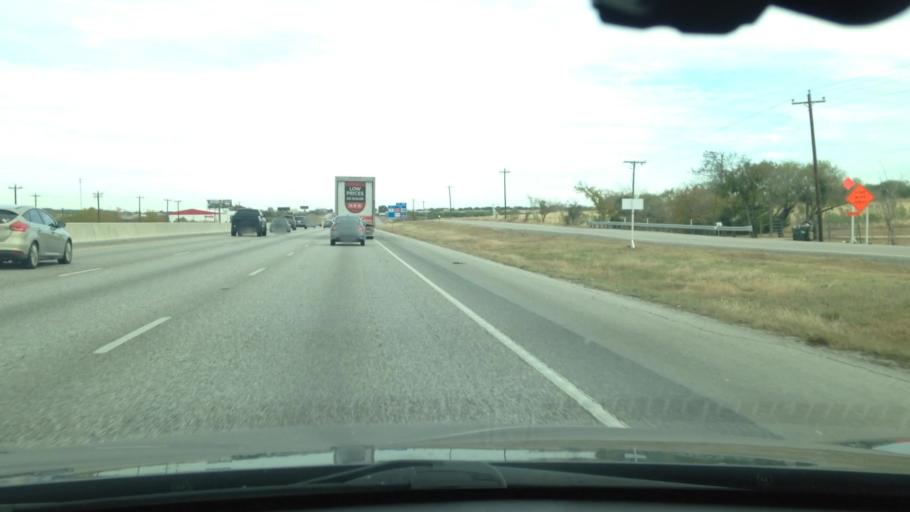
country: US
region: Texas
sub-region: Guadalupe County
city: Redwood
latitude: 29.8060
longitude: -98.0096
